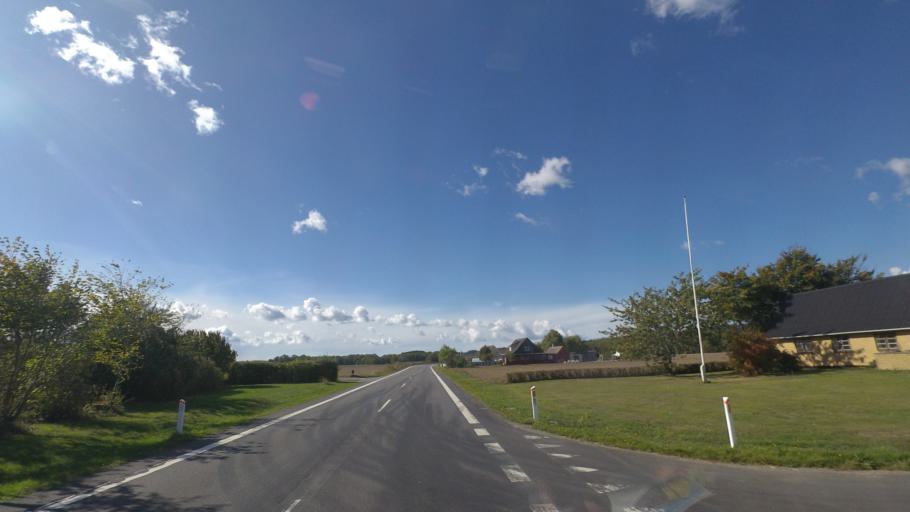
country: DK
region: Capital Region
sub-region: Bornholm Kommune
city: Nexo
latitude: 55.0607
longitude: 15.0512
